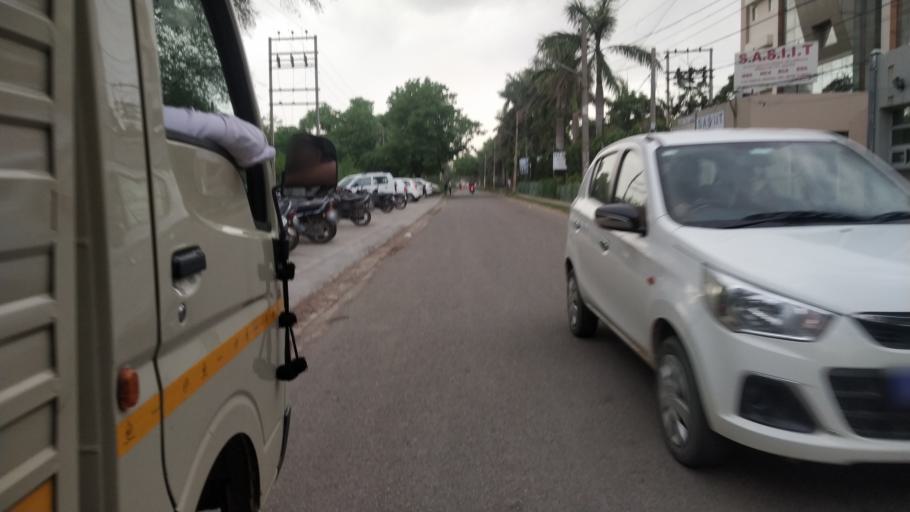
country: IN
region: Punjab
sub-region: Ajitgarh
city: Mohali
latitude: 30.7136
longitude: 76.7084
